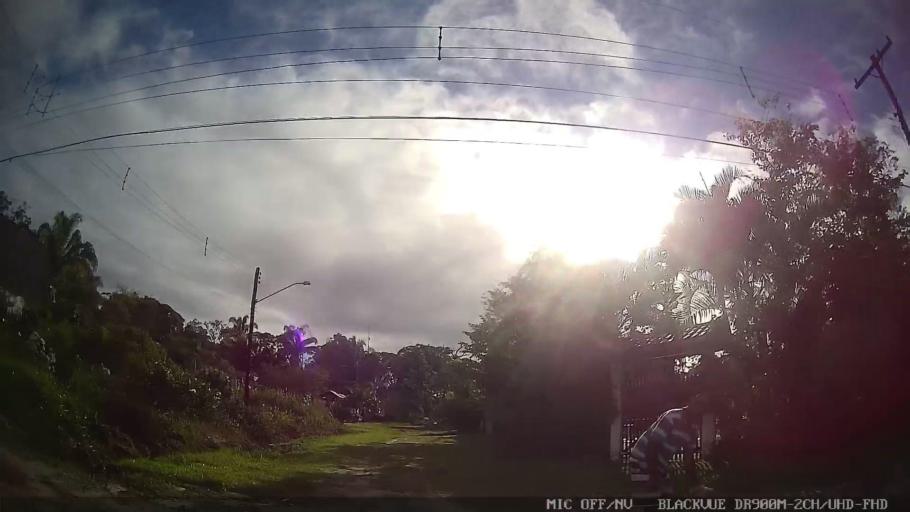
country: BR
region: Sao Paulo
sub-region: Peruibe
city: Peruibe
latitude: -24.2355
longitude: -46.9125
